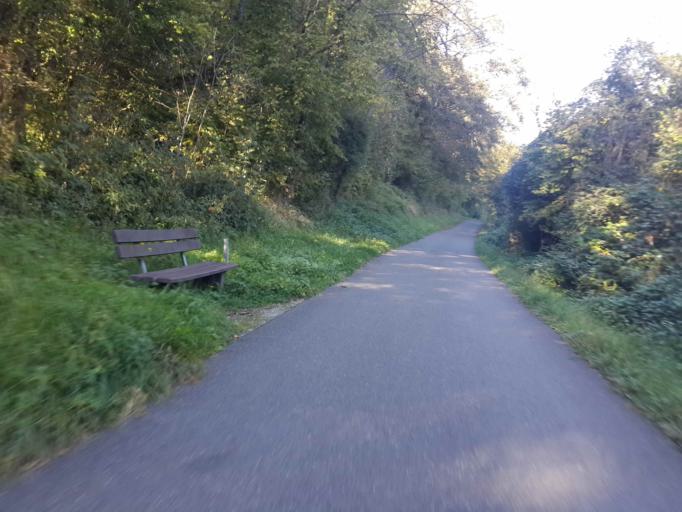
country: DE
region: Baden-Wuerttemberg
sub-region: Regierungsbezirk Stuttgart
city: Wertheim
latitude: 49.7485
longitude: 9.5101
